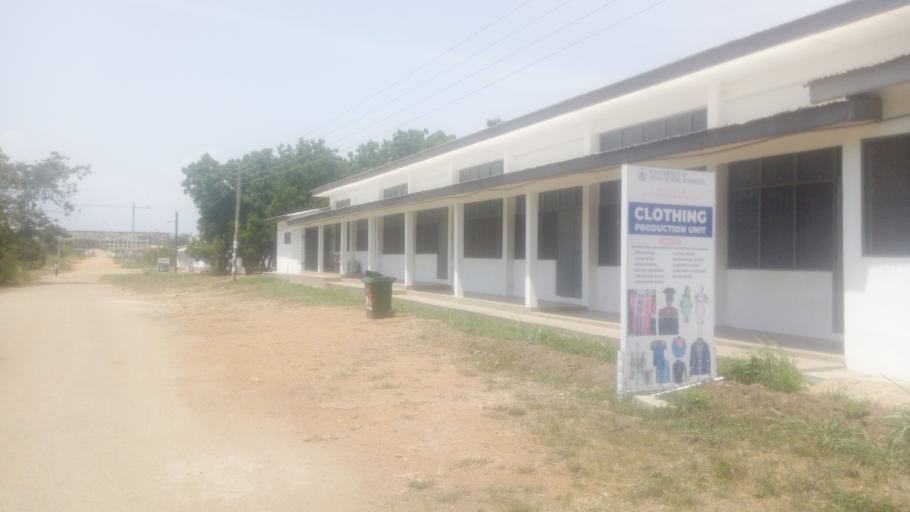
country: GH
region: Central
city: Winneba
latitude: 5.3661
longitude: -0.6332
